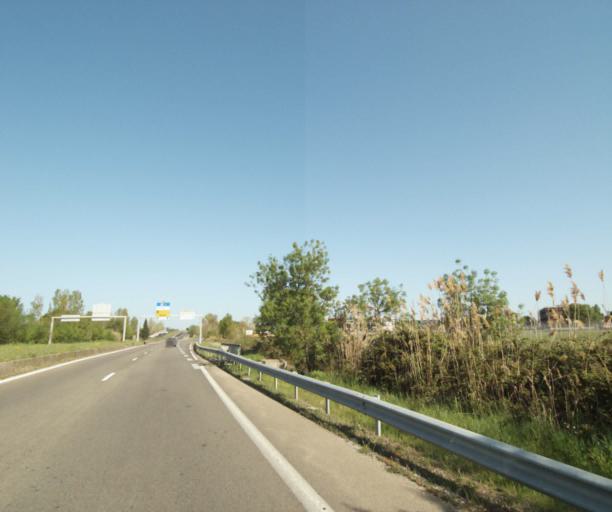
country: FR
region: Languedoc-Roussillon
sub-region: Departement de l'Herault
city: Perols
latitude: 43.5767
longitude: 3.9487
